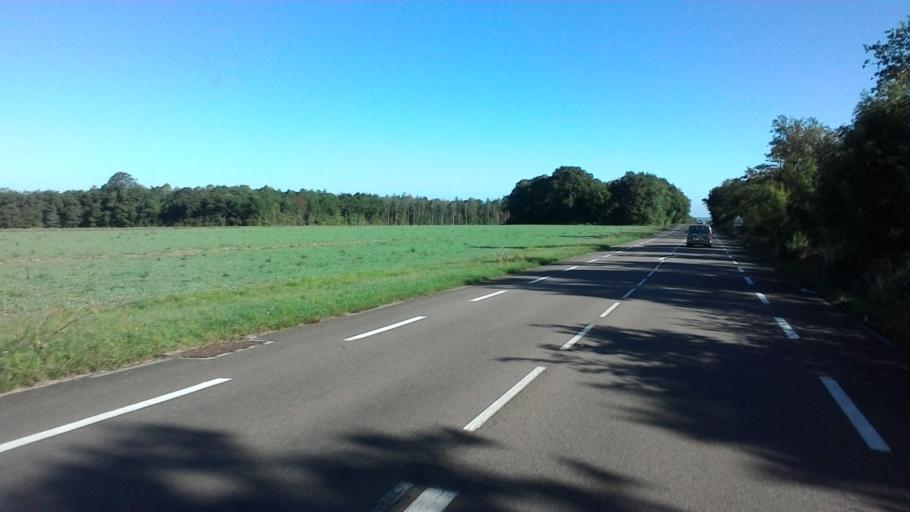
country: FR
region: Bourgogne
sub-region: Departement de la Cote-d'Or
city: Chatillon-sur-Seine
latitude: 47.8180
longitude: 4.5352
